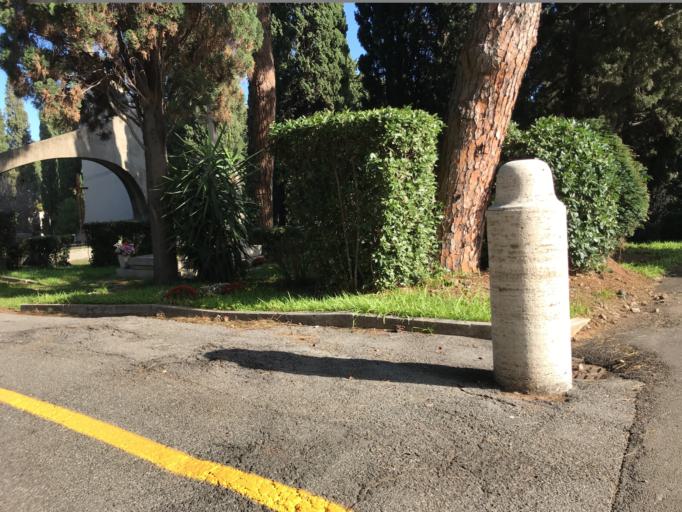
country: IT
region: Latium
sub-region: Citta metropolitana di Roma Capitale
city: Rome
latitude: 41.9040
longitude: 12.5315
